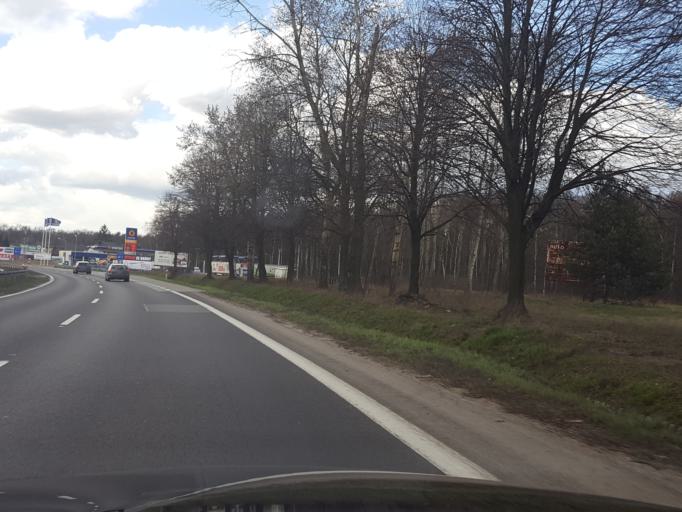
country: PL
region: Silesian Voivodeship
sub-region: Powiat pszczynski
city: Piasek
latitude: 50.0137
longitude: 18.9566
